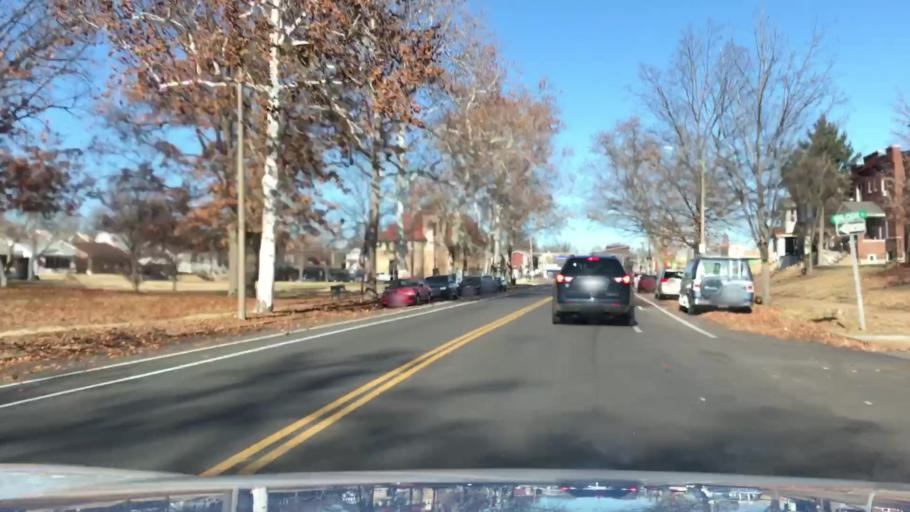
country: US
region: Missouri
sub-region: Saint Louis County
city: Lemay
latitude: 38.5827
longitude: -90.2766
